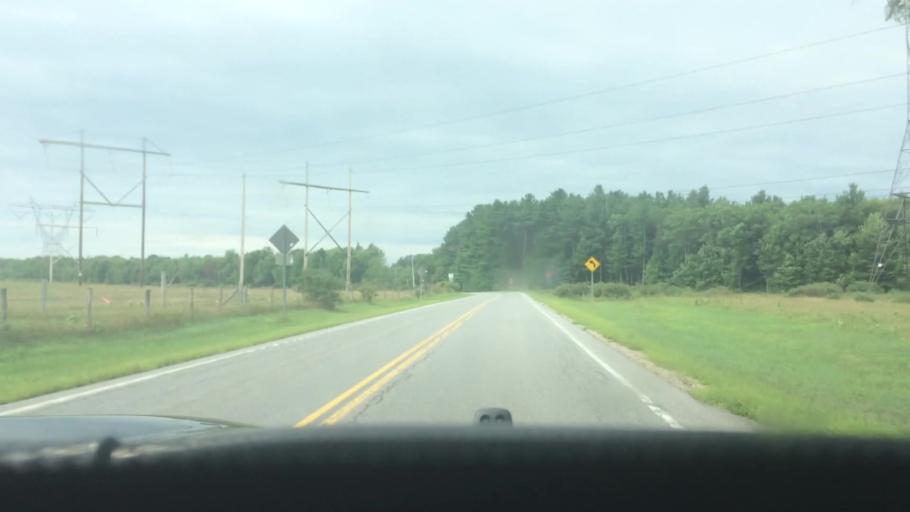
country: US
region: New York
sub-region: St. Lawrence County
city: Canton
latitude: 44.5114
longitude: -75.2066
